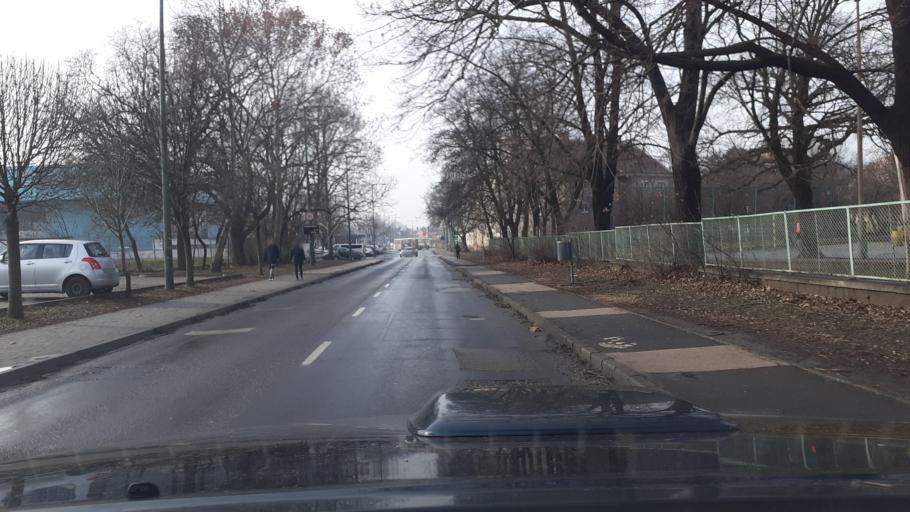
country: HU
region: Fejer
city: Dunaujvaros
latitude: 46.9585
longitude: 18.9399
